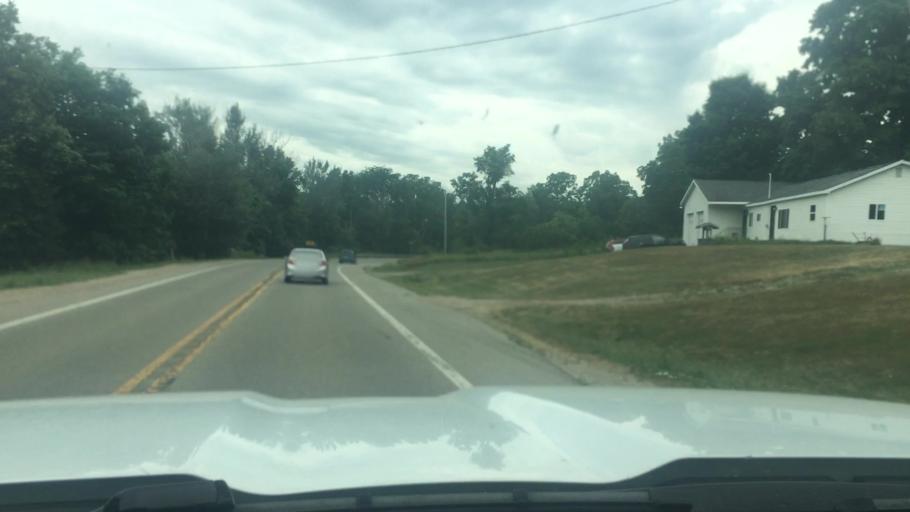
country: US
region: Michigan
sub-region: Ionia County
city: Saranac
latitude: 42.9473
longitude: -85.1883
